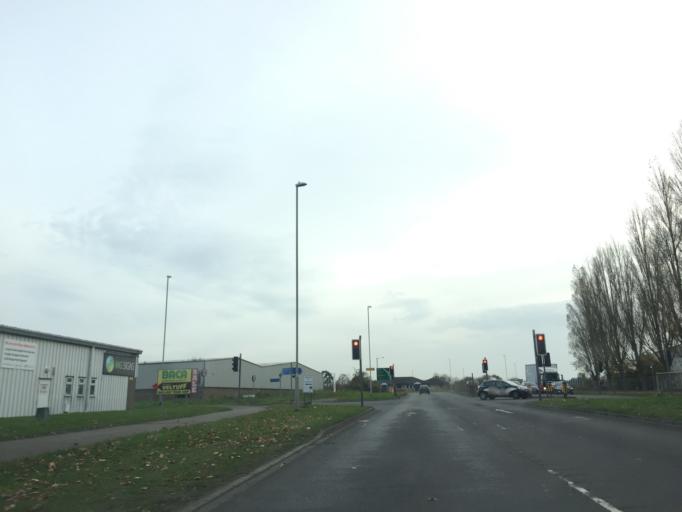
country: GB
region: England
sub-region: Northamptonshire
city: Northampton
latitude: 52.2757
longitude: -0.8648
